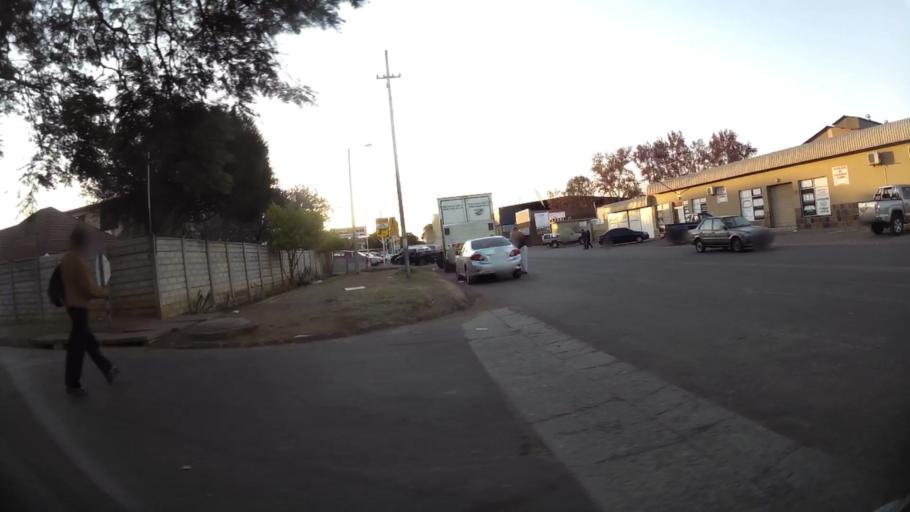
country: ZA
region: North-West
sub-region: Bojanala Platinum District Municipality
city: Rustenburg
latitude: -25.6638
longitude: 27.2484
